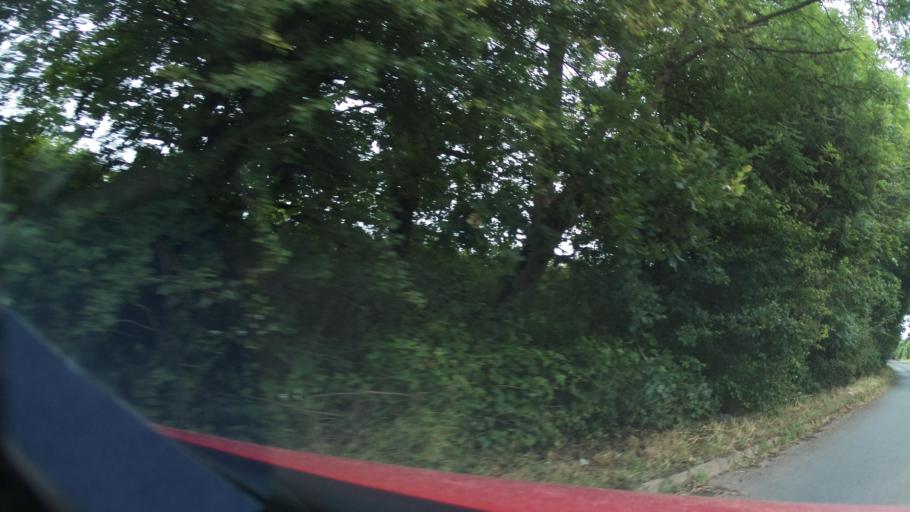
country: GB
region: England
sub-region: Devon
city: Newton Poppleford
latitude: 50.7551
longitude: -3.3469
